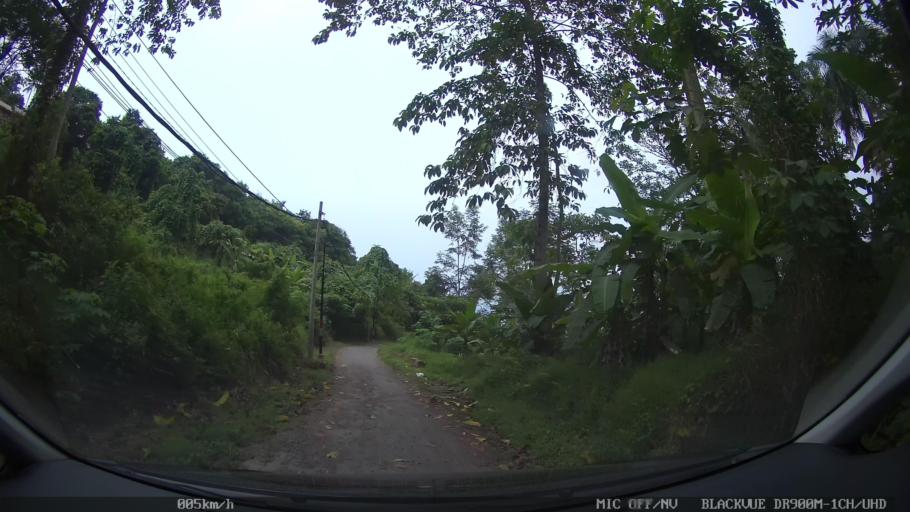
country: ID
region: Lampung
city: Panjang
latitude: -5.4315
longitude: 105.3093
